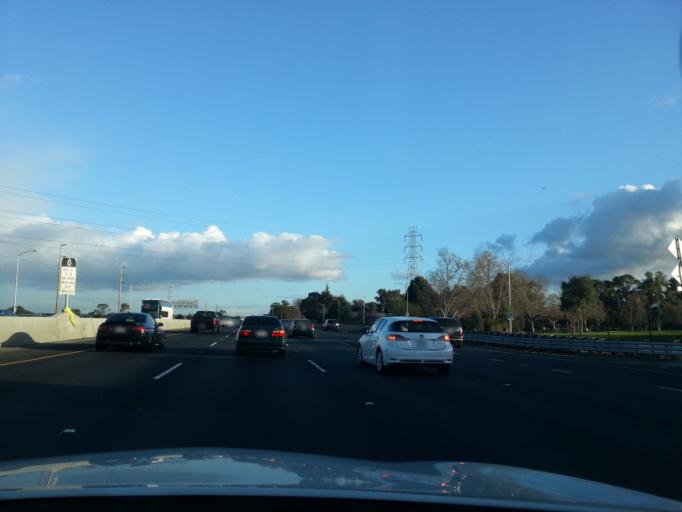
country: US
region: California
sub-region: Santa Clara County
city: Palo Alto
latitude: 37.4445
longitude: -122.1186
